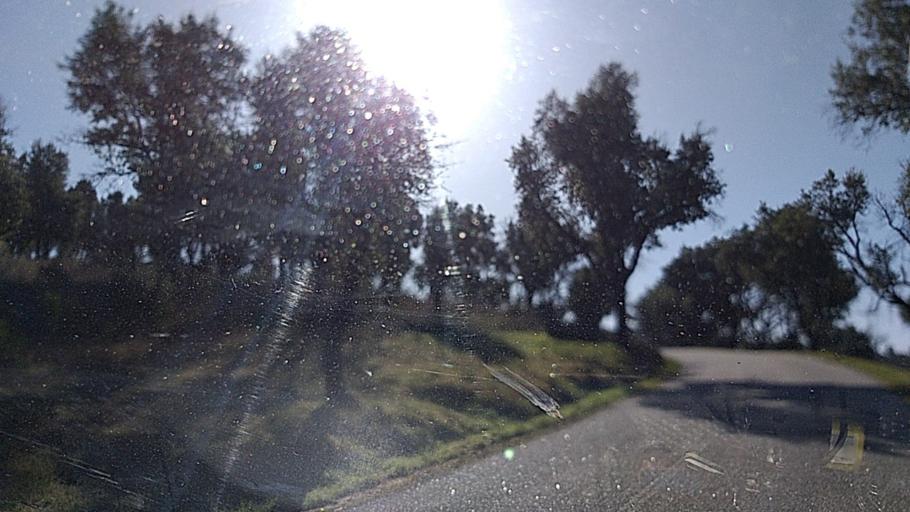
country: PT
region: Guarda
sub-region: Celorico da Beira
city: Celorico da Beira
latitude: 40.6944
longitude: -7.4497
